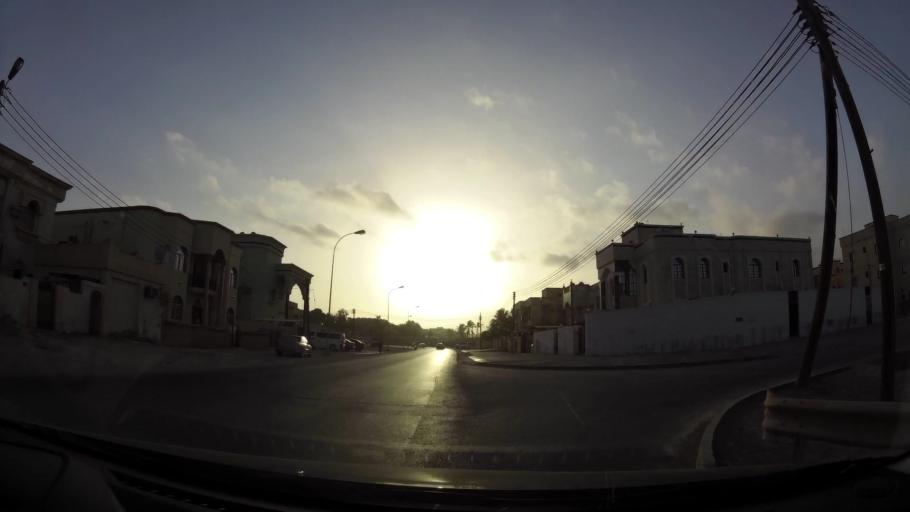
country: OM
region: Zufar
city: Salalah
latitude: 17.0030
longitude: 54.0350
